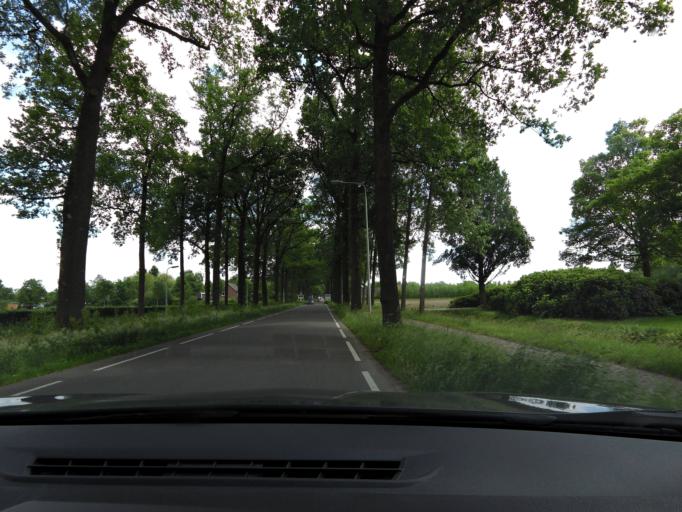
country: NL
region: North Brabant
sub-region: Gemeente Loon op Zand
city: Loon op Zand
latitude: 51.6137
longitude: 5.1335
